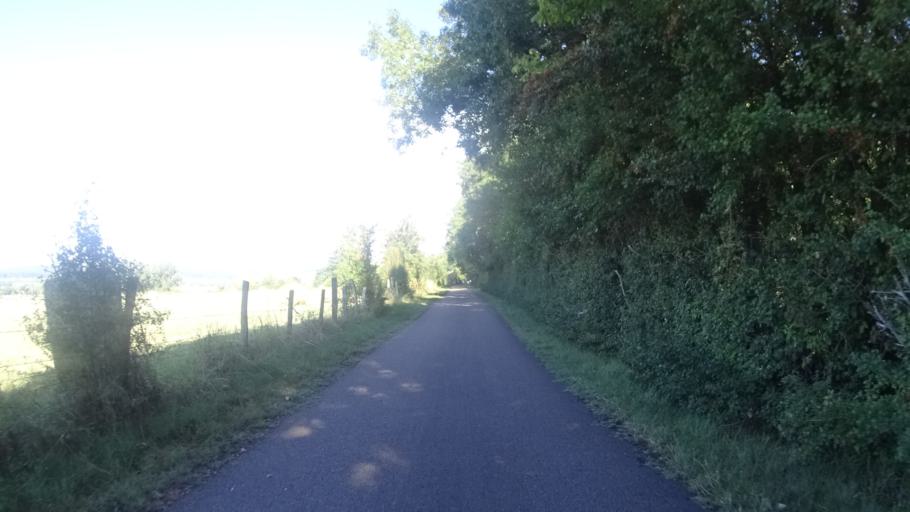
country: FR
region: Centre
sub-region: Departement du Cher
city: Sancerre
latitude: 47.3095
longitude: 2.8926
